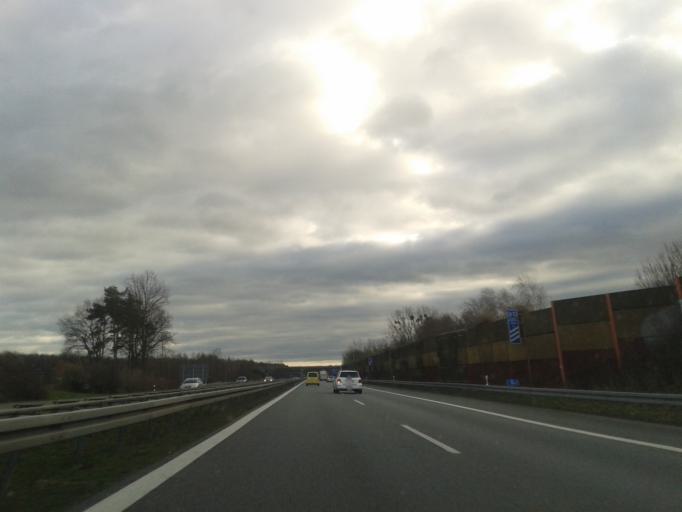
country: DE
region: Saxony
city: Lichtenberg
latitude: 51.1596
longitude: 13.9680
